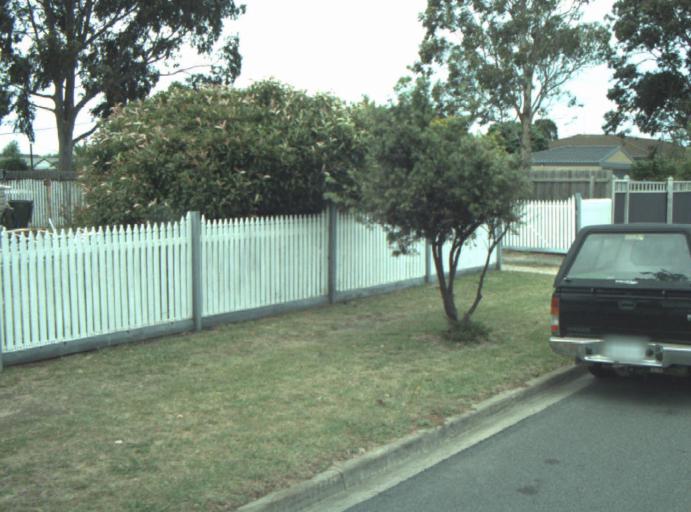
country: AU
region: Victoria
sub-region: Greater Geelong
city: Leopold
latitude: -38.1873
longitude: 144.4743
